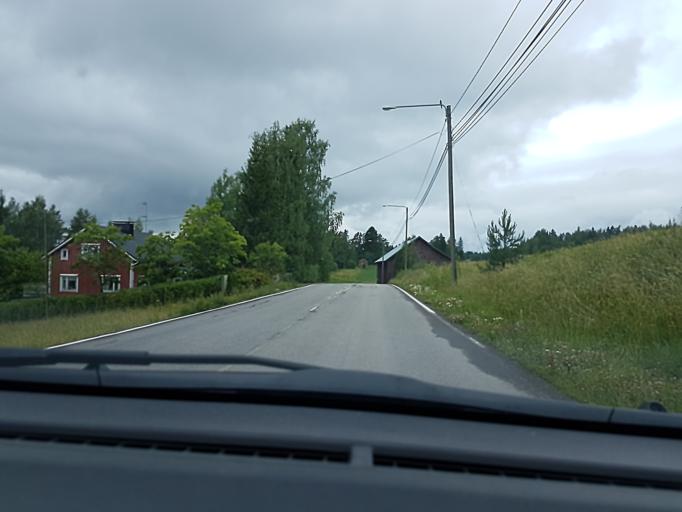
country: FI
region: Uusimaa
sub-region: Helsinki
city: Pornainen
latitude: 60.4339
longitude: 25.3946
